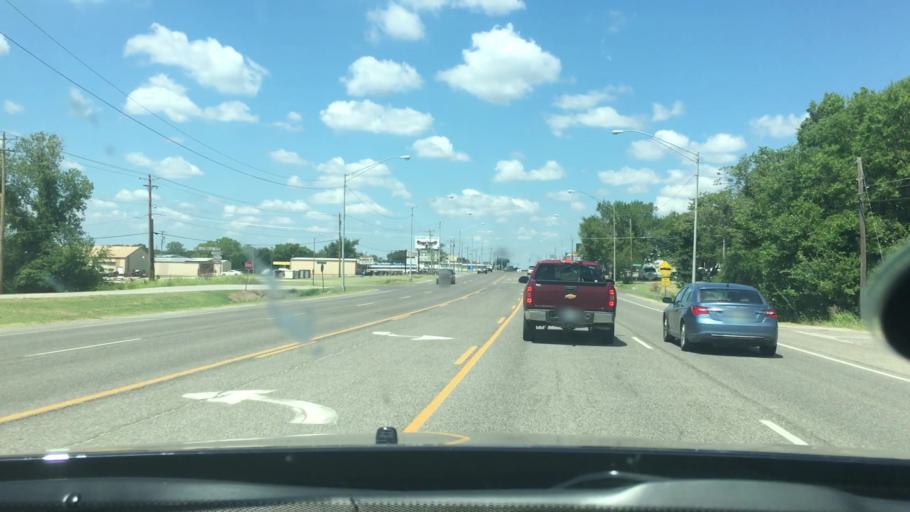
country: US
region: Oklahoma
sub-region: Carter County
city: Lone Grove
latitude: 34.1730
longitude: -97.2552
